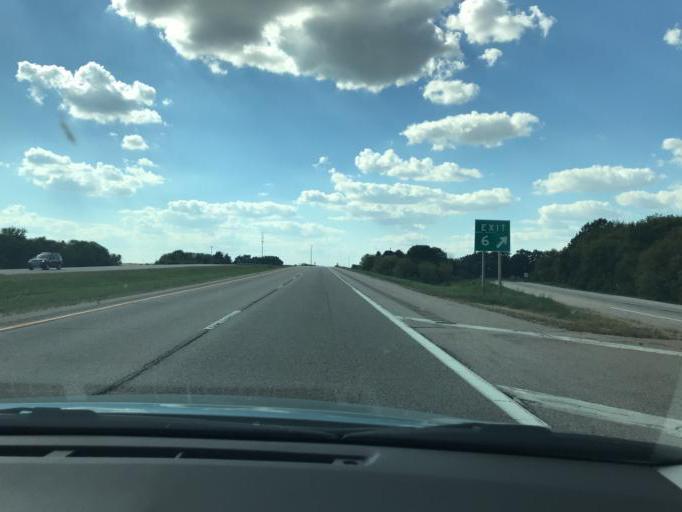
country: US
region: Wisconsin
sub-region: Rock County
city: Clinton
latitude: 42.5728
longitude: -88.8600
